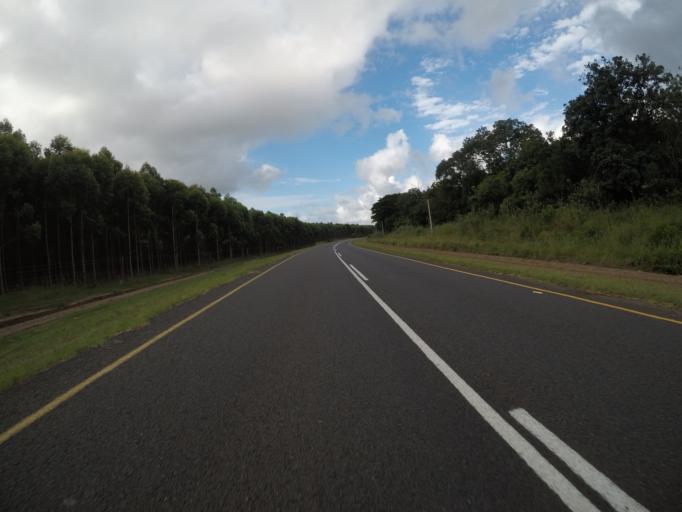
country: ZA
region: KwaZulu-Natal
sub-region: uMkhanyakude District Municipality
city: Mtubatuba
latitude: -28.3718
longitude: 32.2546
